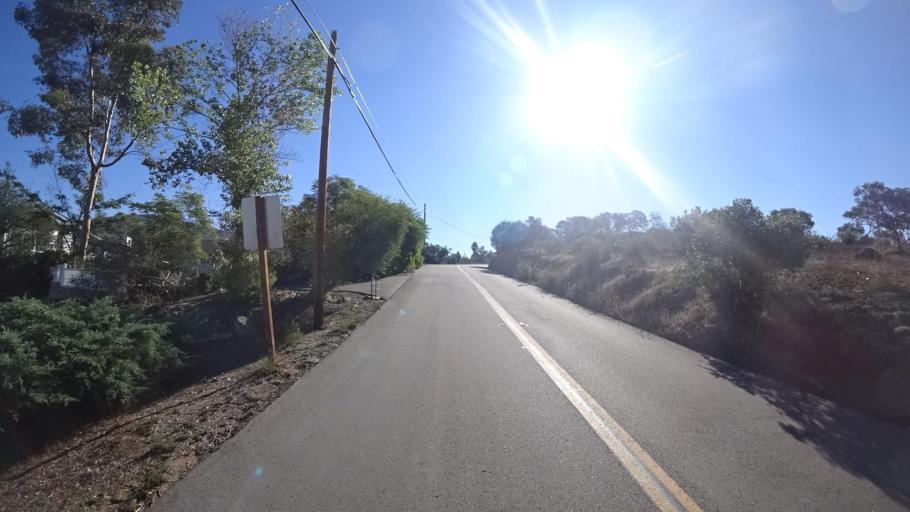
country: US
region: California
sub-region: San Diego County
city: Alpine
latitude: 32.8340
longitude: -116.7633
